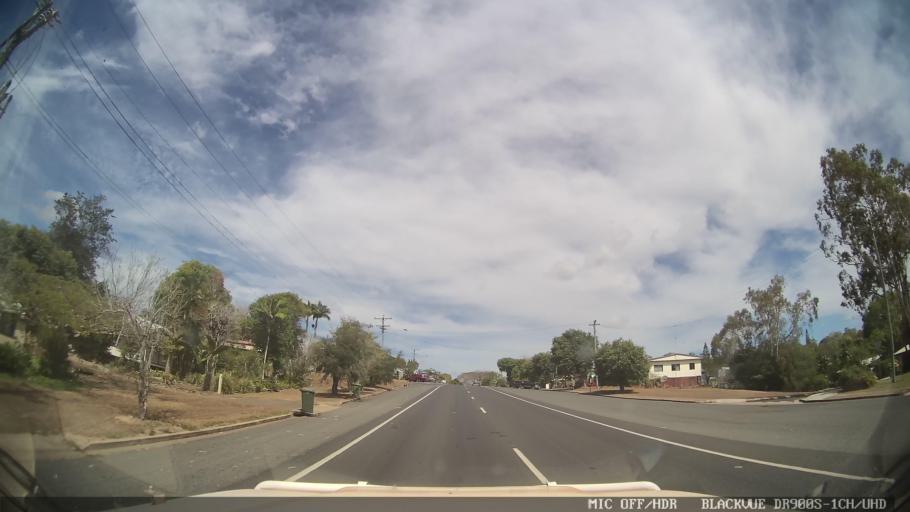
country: AU
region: Queensland
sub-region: Cairns
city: Port Douglas
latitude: -16.6726
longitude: 145.3293
